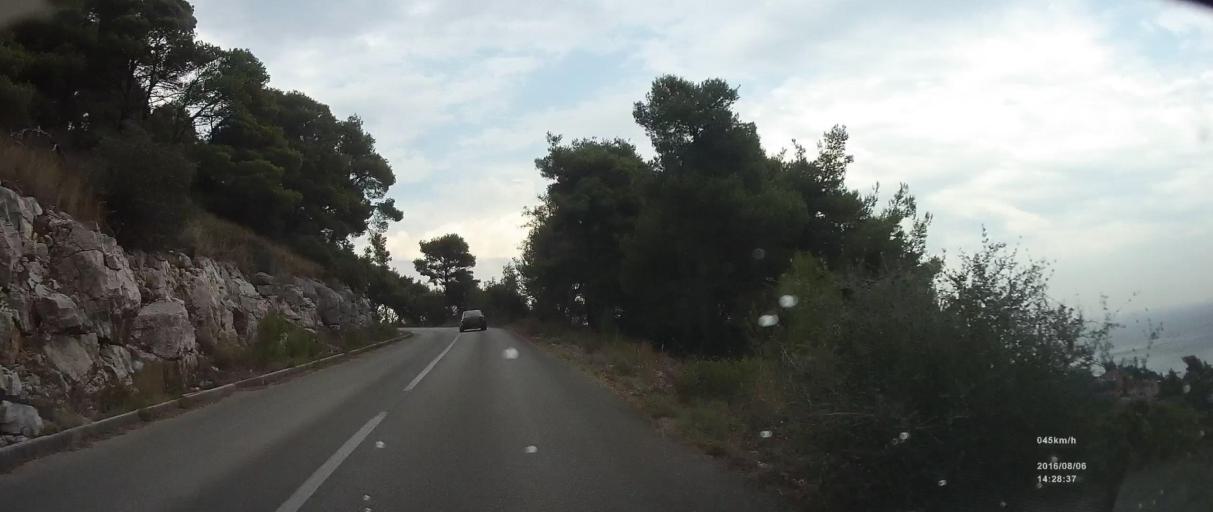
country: HR
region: Dubrovacko-Neretvanska
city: Ston
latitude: 42.7048
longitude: 17.7372
